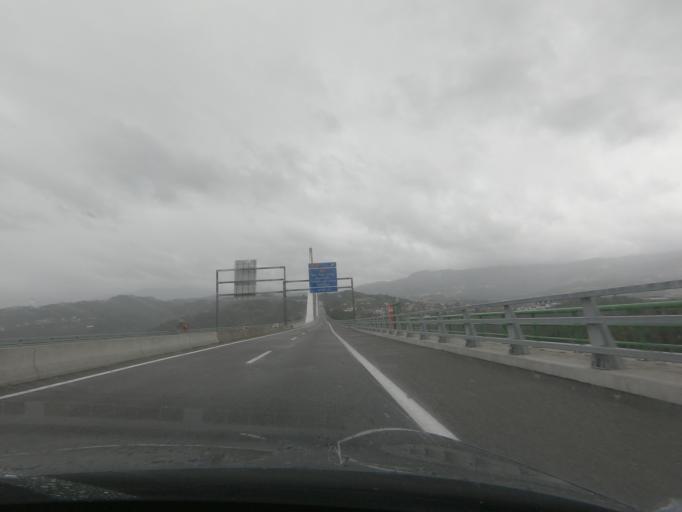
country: PT
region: Vila Real
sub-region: Vila Real
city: Vila Real
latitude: 41.2780
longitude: -7.7454
